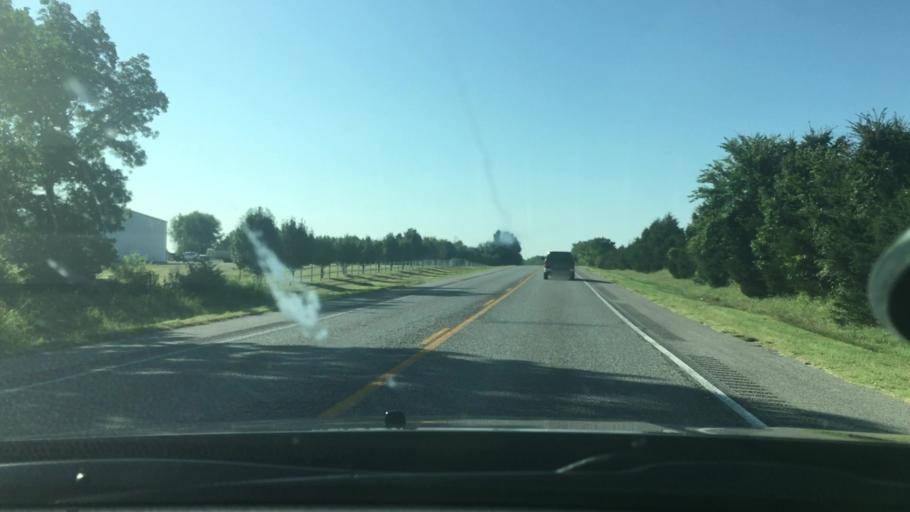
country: US
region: Oklahoma
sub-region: Johnston County
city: Tishomingo
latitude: 34.2517
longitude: -96.7610
